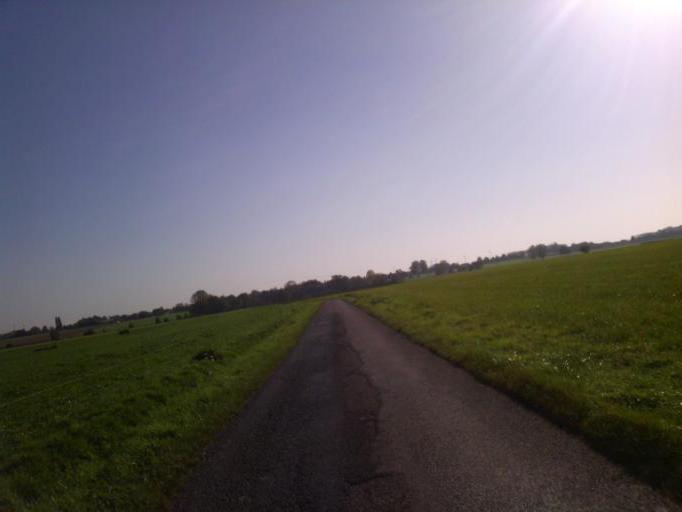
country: BE
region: Wallonia
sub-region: Province du Hainaut
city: Peruwelz
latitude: 50.5849
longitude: 3.5600
